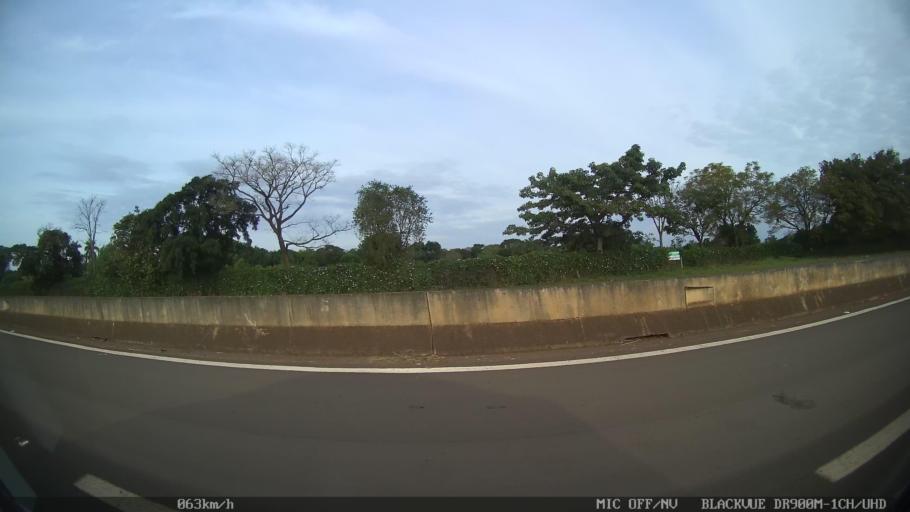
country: BR
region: Sao Paulo
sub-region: Iracemapolis
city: Iracemapolis
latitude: -22.5915
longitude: -47.4627
